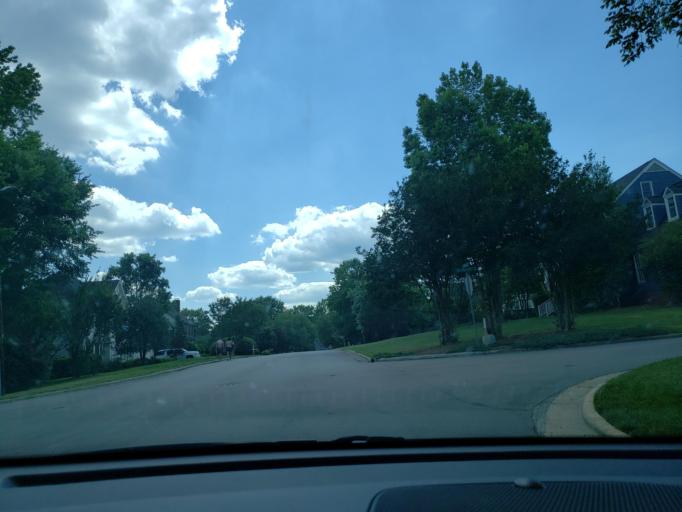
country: US
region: North Carolina
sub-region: Orange County
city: Chapel Hill
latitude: 35.9697
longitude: -78.9862
